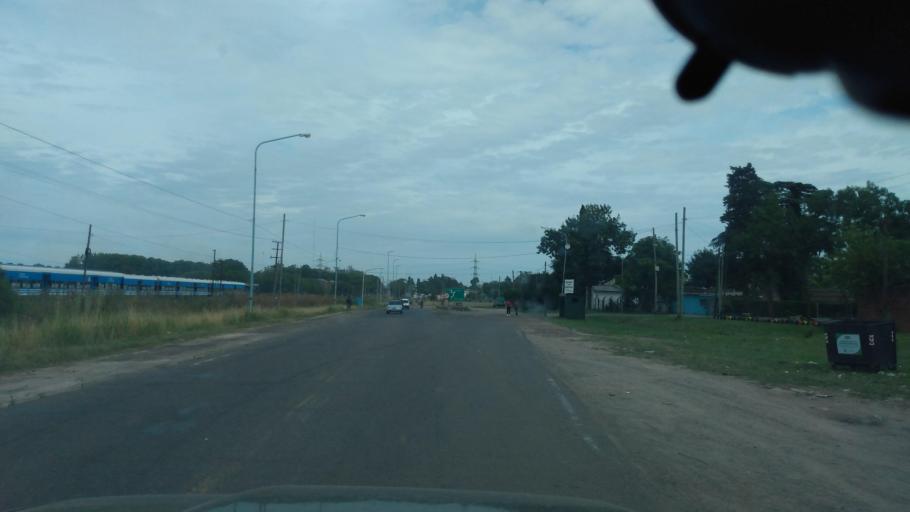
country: AR
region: Buenos Aires
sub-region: Partido de Lujan
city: Lujan
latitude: -34.5788
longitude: -59.0799
